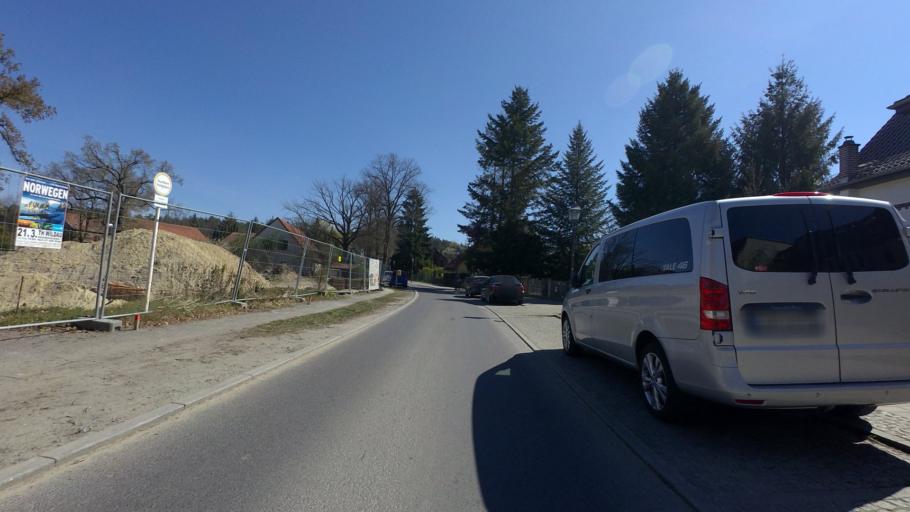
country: DE
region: Brandenburg
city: Zeuthen
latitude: 52.3406
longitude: 13.6139
